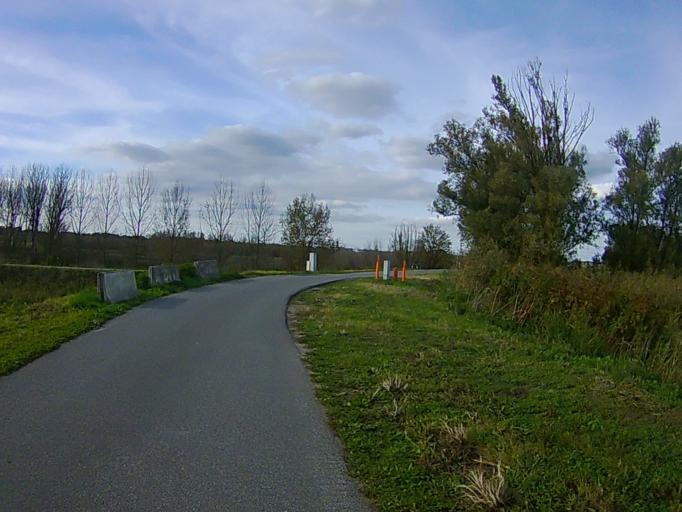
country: BE
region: Flanders
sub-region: Provincie Oost-Vlaanderen
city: Kruibeke
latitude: 51.1589
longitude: 4.3258
